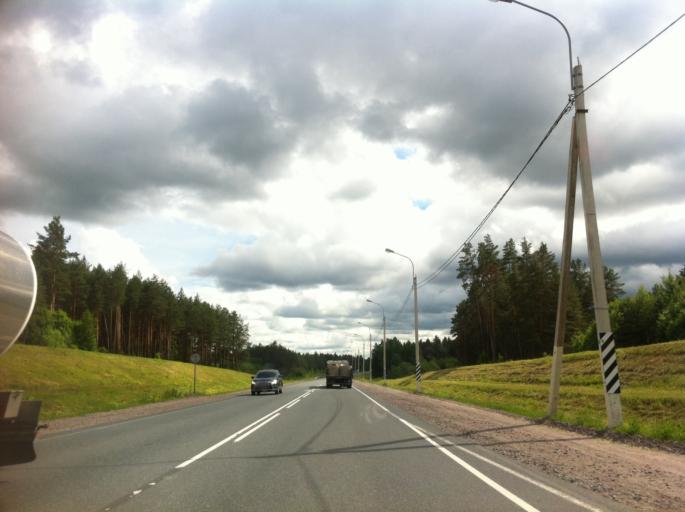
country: RU
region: Leningrad
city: Luga
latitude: 58.7112
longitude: 29.8797
